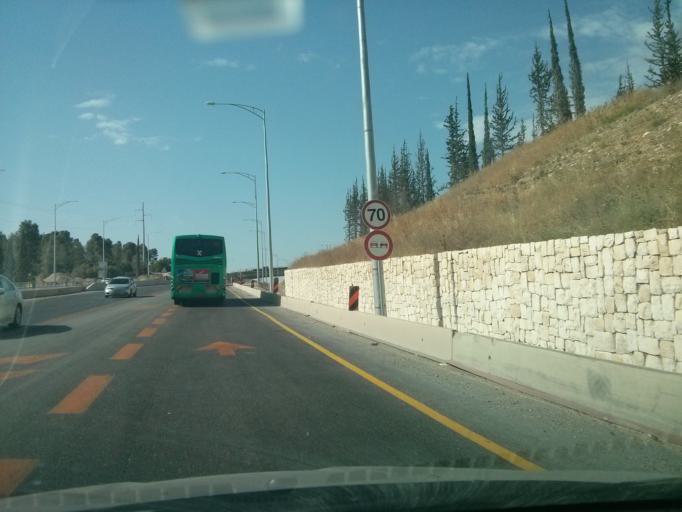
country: IL
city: Mevo horon
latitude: 31.7971
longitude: 35.0147
